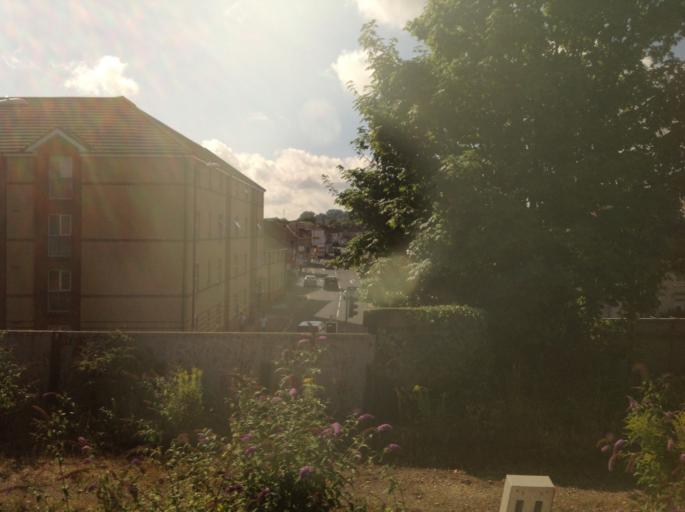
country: GB
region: England
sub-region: Borough of Swindon
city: Swindon
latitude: 51.5666
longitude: -1.7824
